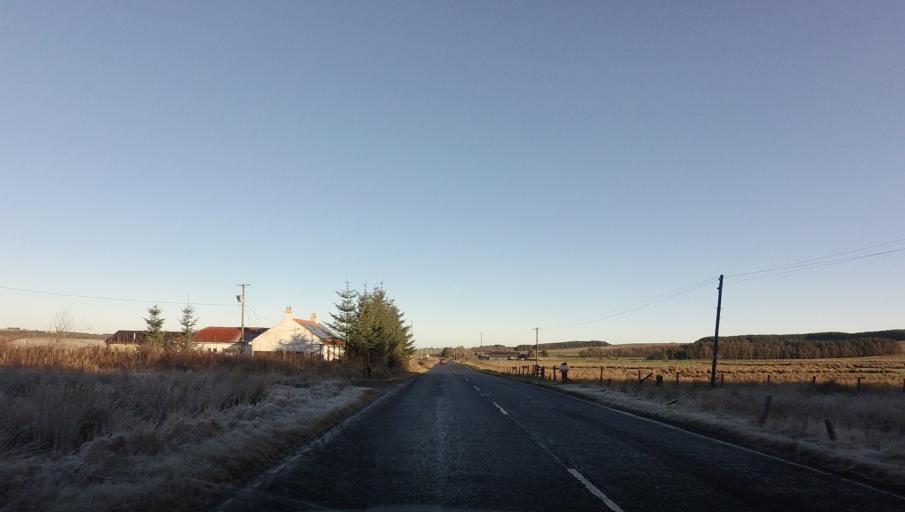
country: GB
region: Scotland
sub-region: West Lothian
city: Fauldhouse
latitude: 55.8198
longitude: -3.6910
